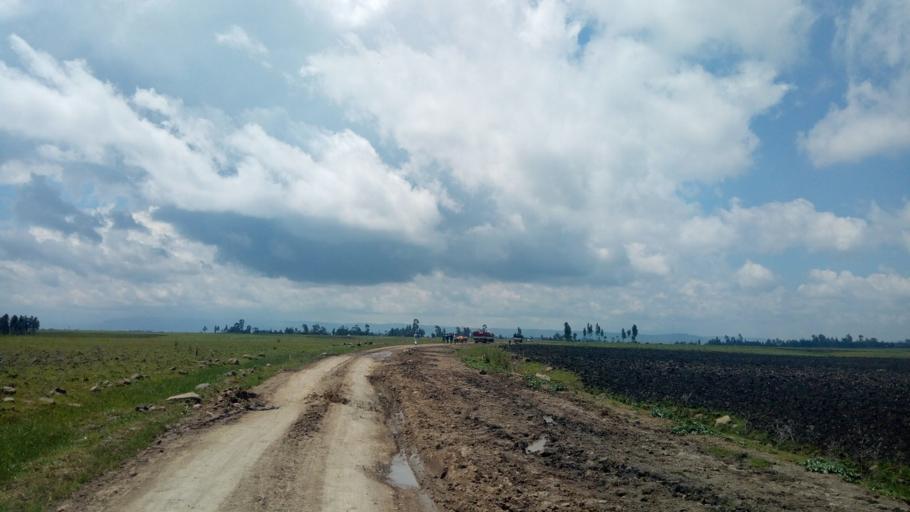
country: ET
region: Oromiya
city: Sendafa
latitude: 9.0085
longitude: 39.1224
